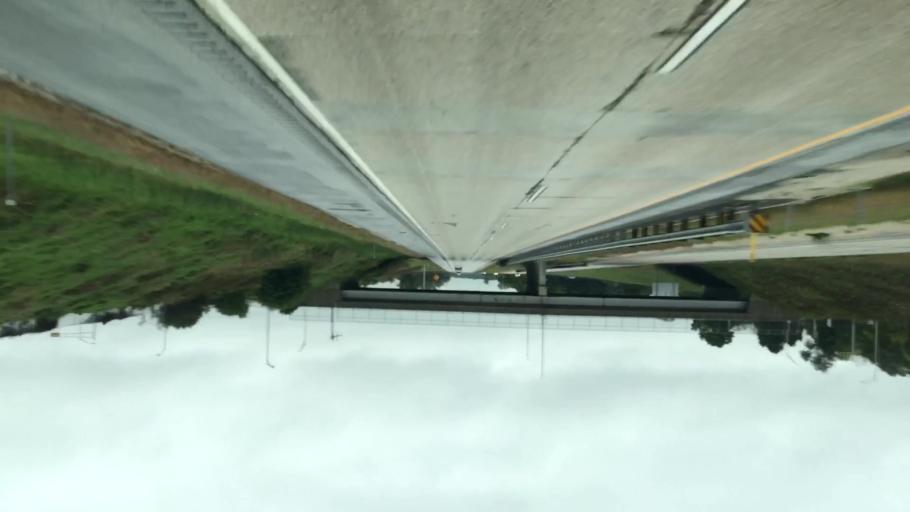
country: US
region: Wisconsin
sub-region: Waukesha County
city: Pewaukee
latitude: 43.0727
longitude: -88.2516
